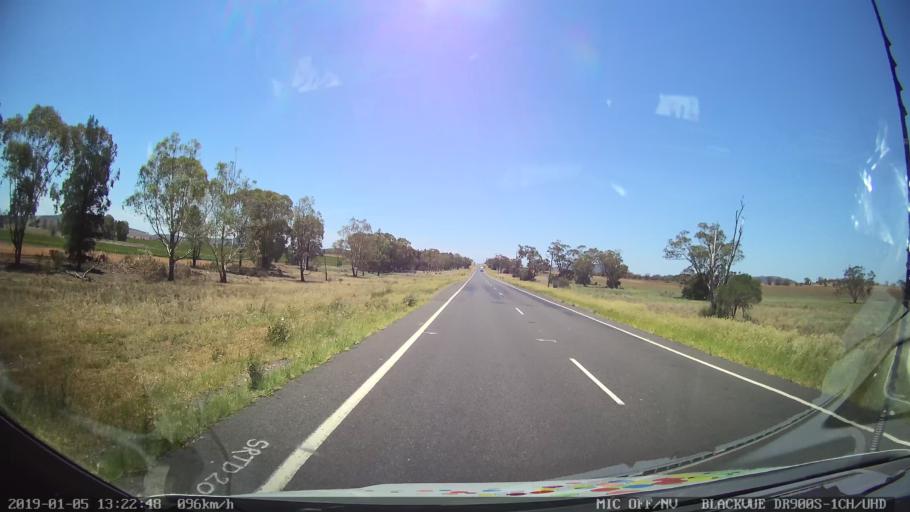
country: AU
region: New South Wales
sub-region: Gunnedah
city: Gunnedah
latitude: -31.0832
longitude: 149.9667
